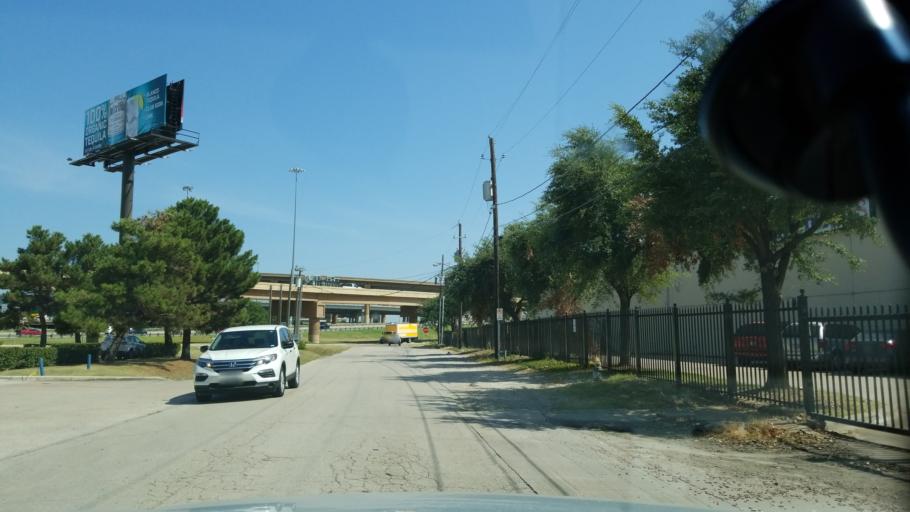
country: US
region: Texas
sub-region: Dallas County
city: Farmers Branch
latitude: 32.9049
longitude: -96.8958
